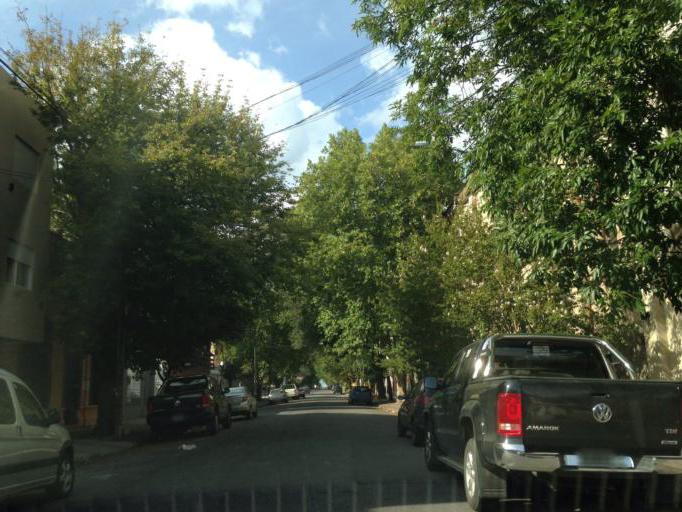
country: AR
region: Buenos Aires
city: Mar del Plata
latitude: -37.9888
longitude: -57.5498
